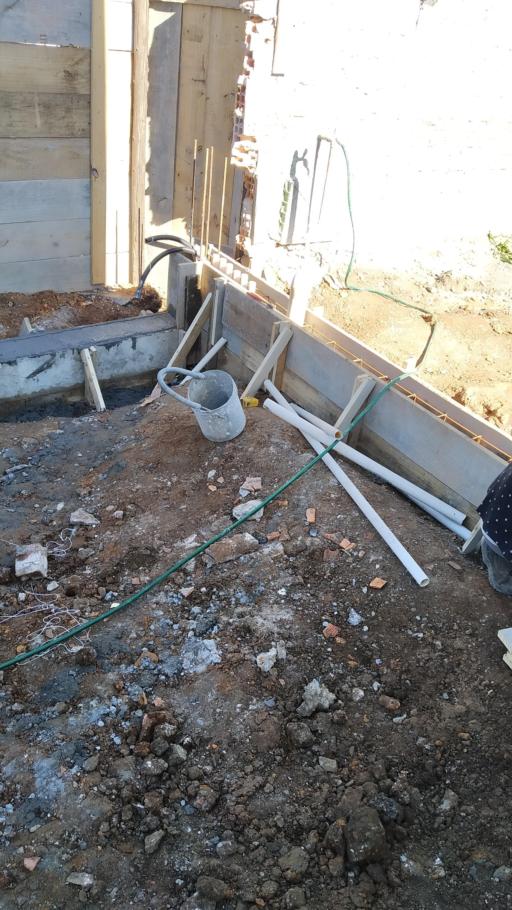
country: BR
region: Santa Catarina
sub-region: Curitibanos
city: Curitibanos
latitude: -27.2950
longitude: -50.5771
